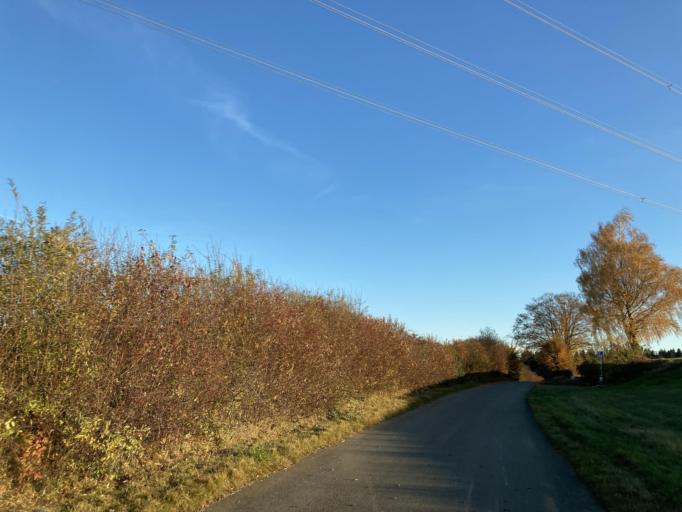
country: DE
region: Baden-Wuerttemberg
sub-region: Tuebingen Region
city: Hirrlingen
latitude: 48.4443
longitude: 8.8864
